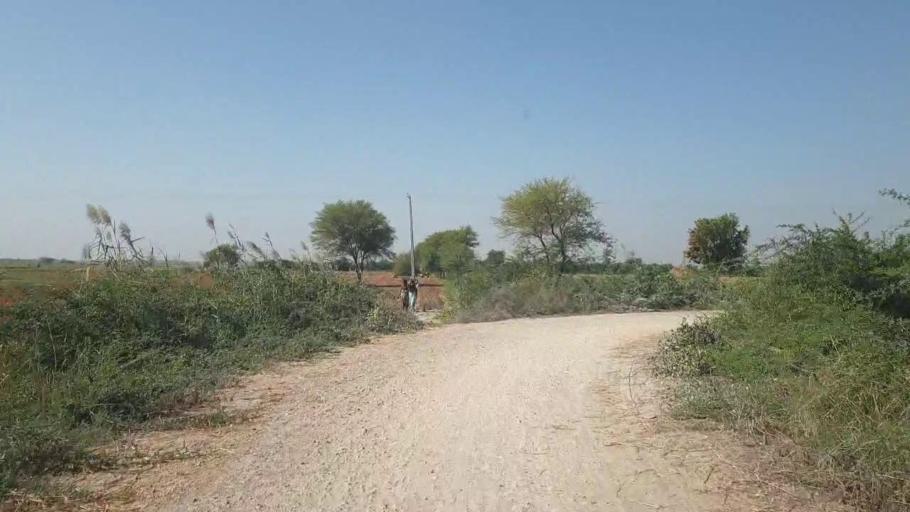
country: PK
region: Sindh
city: Talhar
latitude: 24.7940
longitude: 68.7956
